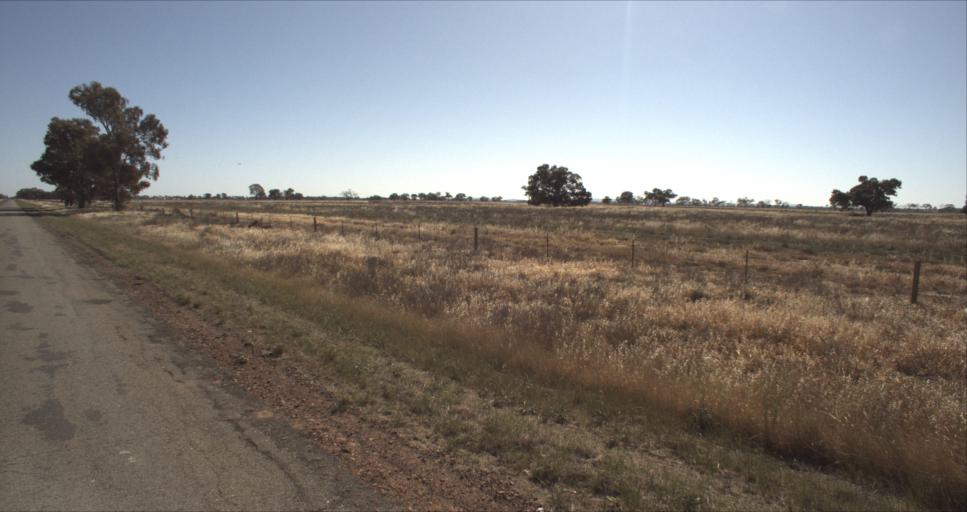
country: AU
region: New South Wales
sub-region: Leeton
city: Leeton
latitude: -34.5995
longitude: 146.2580
